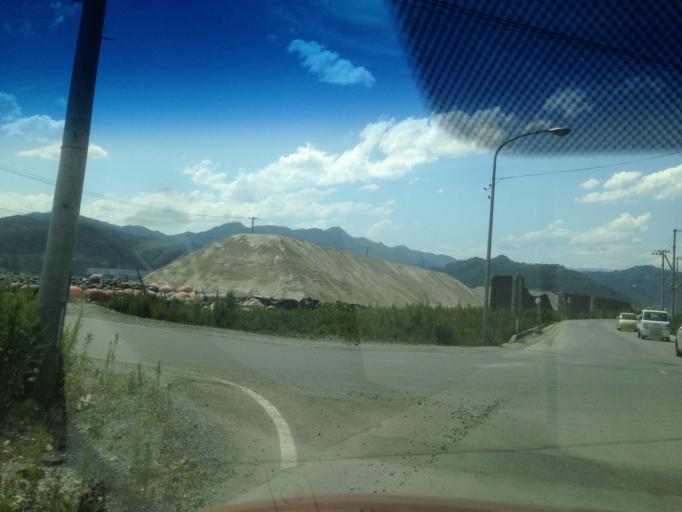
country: JP
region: Iwate
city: Otsuchi
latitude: 39.3555
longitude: 141.9217
